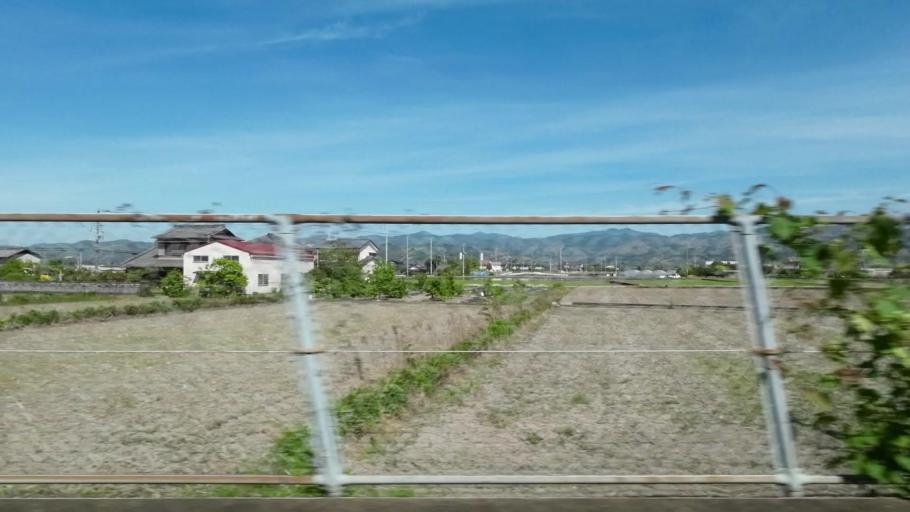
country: JP
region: Kochi
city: Kochi-shi
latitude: 33.5924
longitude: 133.6630
